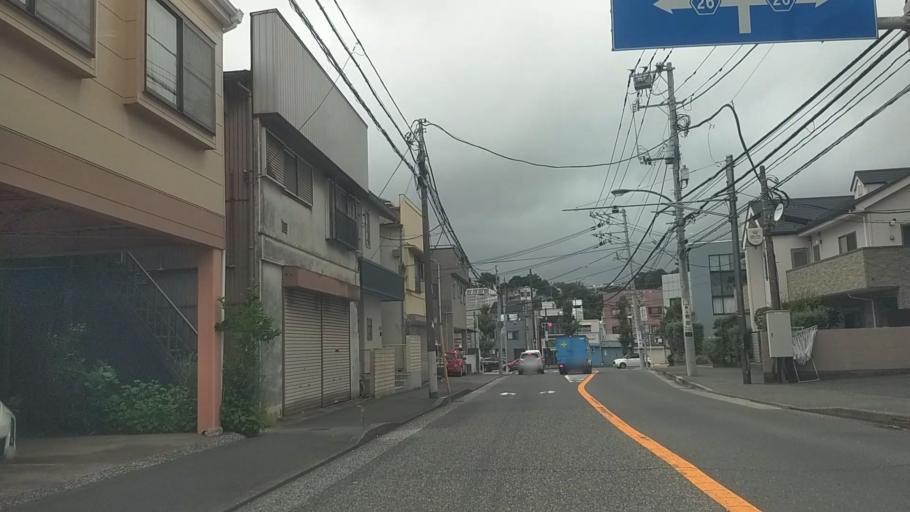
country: JP
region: Kanagawa
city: Yokosuka
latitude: 35.2718
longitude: 139.6730
